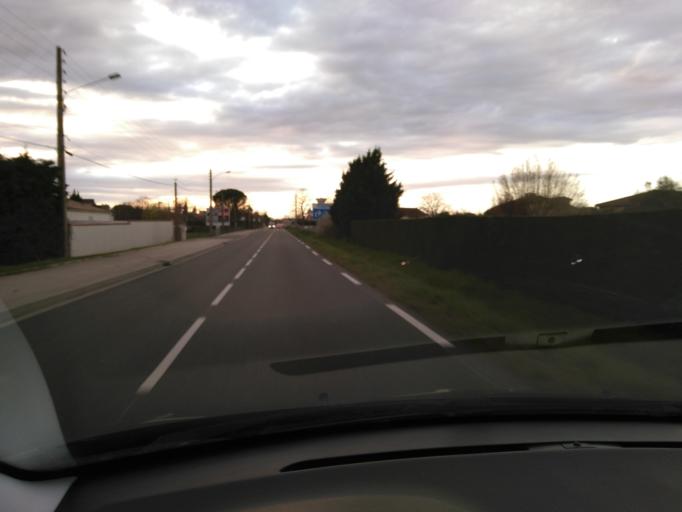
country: FR
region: Midi-Pyrenees
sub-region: Departement de la Haute-Garonne
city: Pibrac
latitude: 43.6076
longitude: 1.2695
